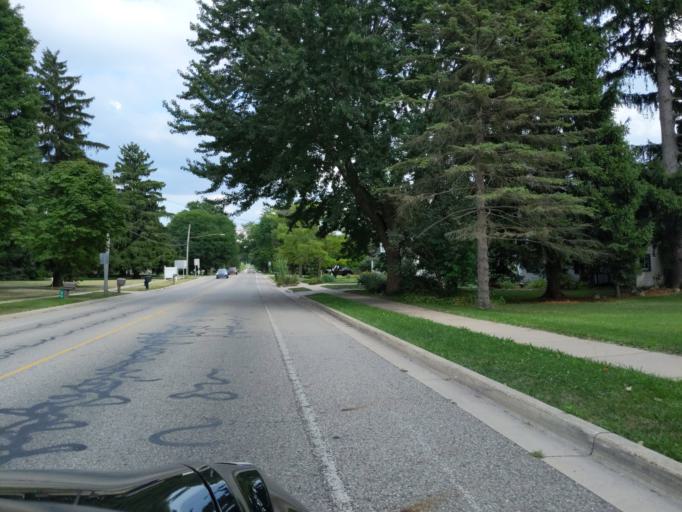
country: US
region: Michigan
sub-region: Clinton County
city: DeWitt
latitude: 42.8353
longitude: -84.5589
